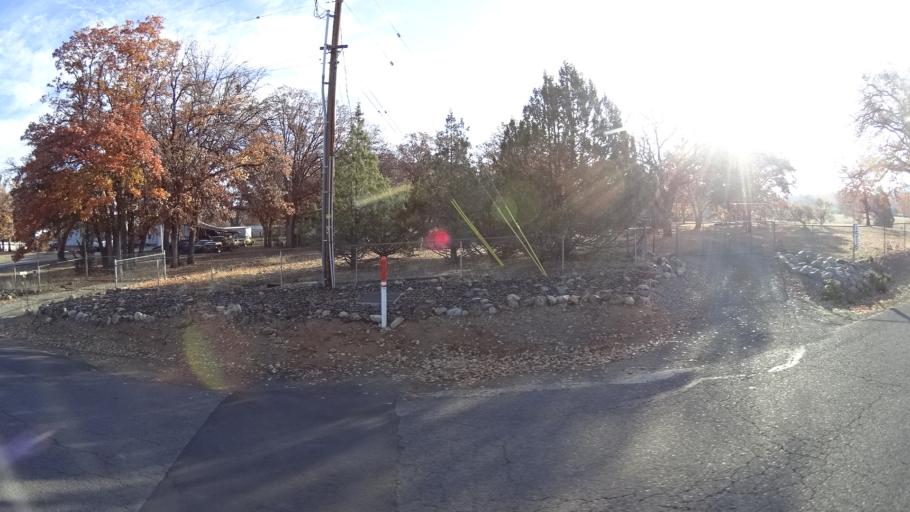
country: US
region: California
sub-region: Siskiyou County
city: Yreka
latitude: 41.7087
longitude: -122.6192
